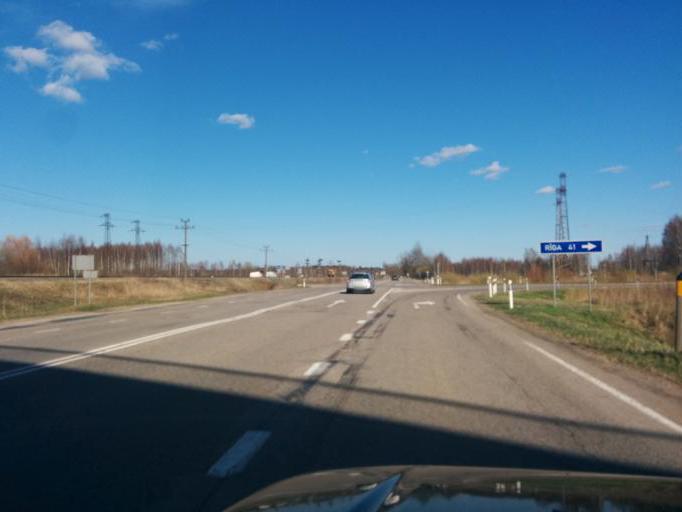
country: LV
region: Ozolnieku
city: Ozolnieki
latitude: 56.6522
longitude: 23.8014
